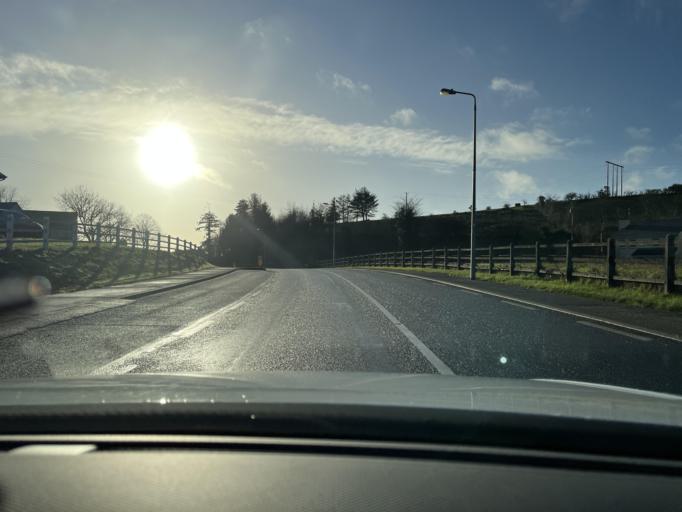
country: IE
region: Connaught
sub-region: County Leitrim
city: Manorhamilton
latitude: 54.2313
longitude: -8.2092
